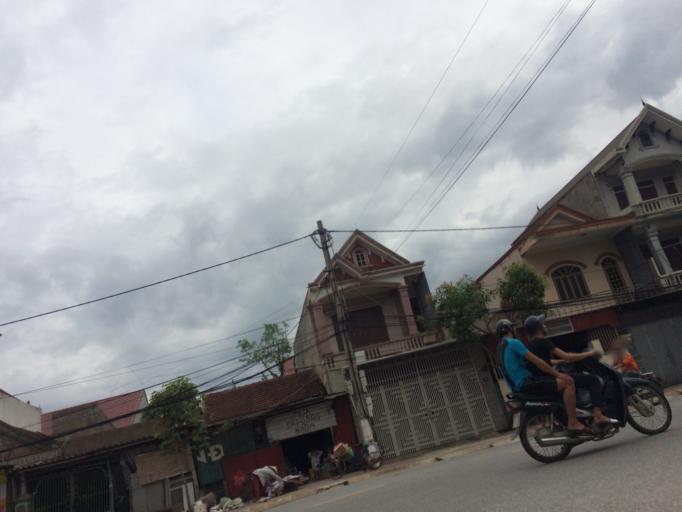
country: VN
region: Ha Tinh
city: Ha Tinh
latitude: 18.3411
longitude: 105.8870
